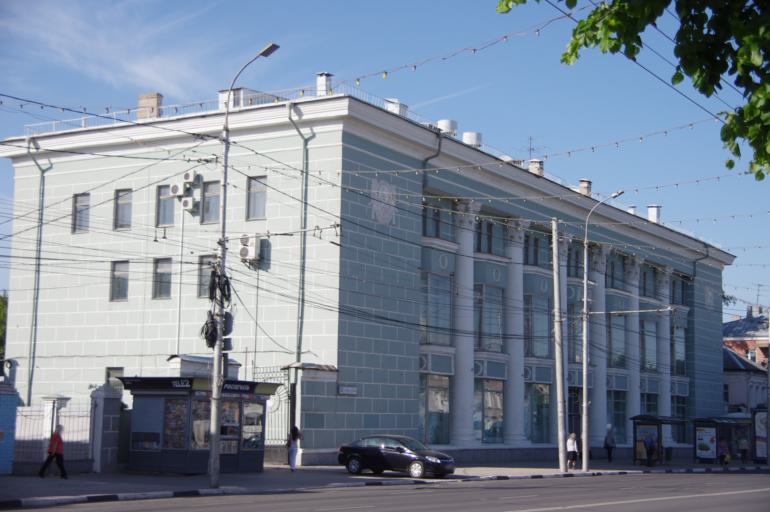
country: RU
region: Rjazan
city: Ryazan'
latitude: 54.6303
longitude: 39.7381
